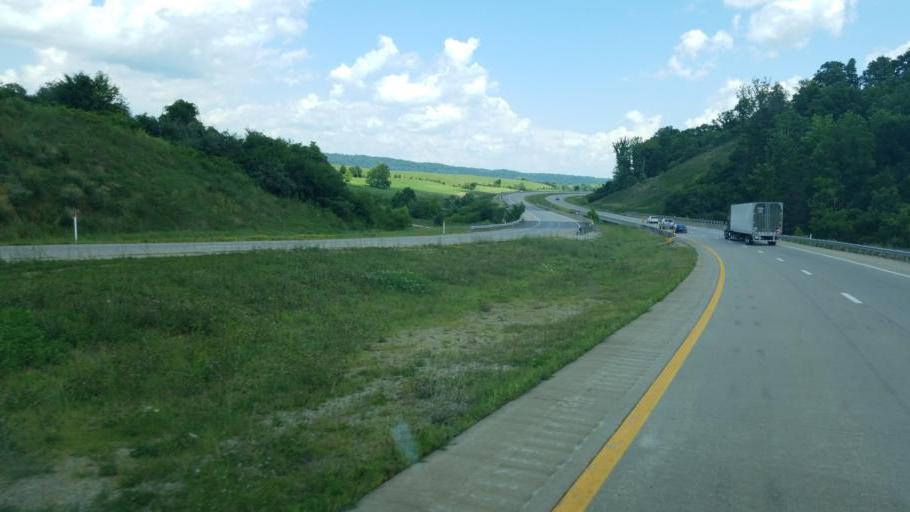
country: US
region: West Virginia
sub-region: Mason County
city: Point Pleasant
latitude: 38.7704
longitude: -82.0508
